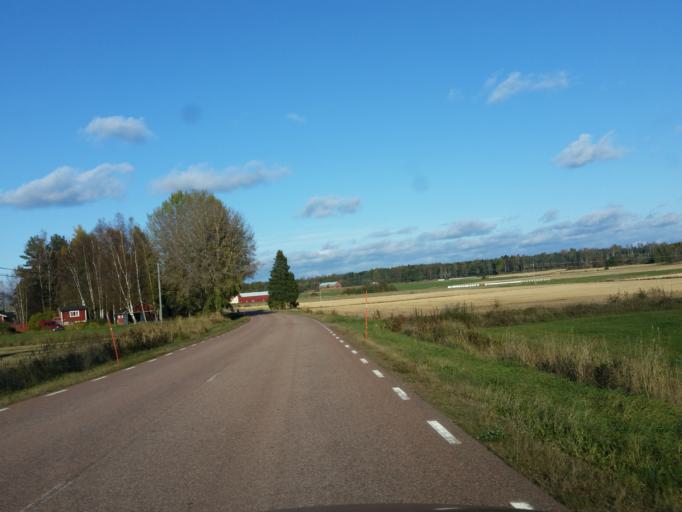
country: AX
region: Mariehamns stad
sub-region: Mariehamn
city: Mariehamn
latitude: 60.1458
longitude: 19.8628
